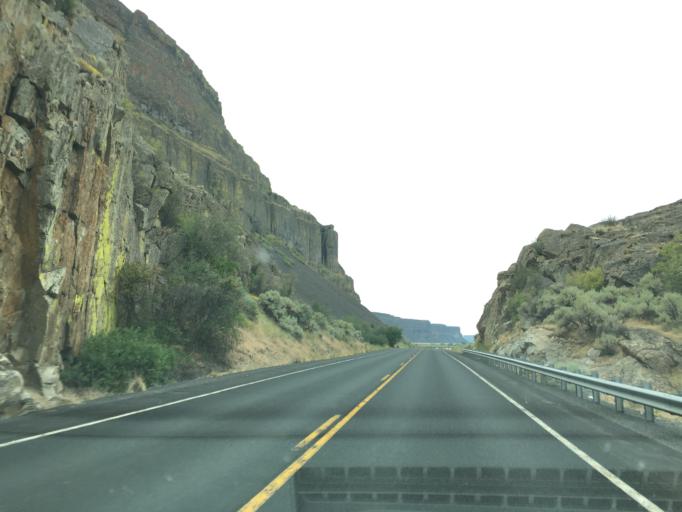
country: US
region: Washington
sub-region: Okanogan County
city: Coulee Dam
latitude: 47.8512
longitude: -119.1129
